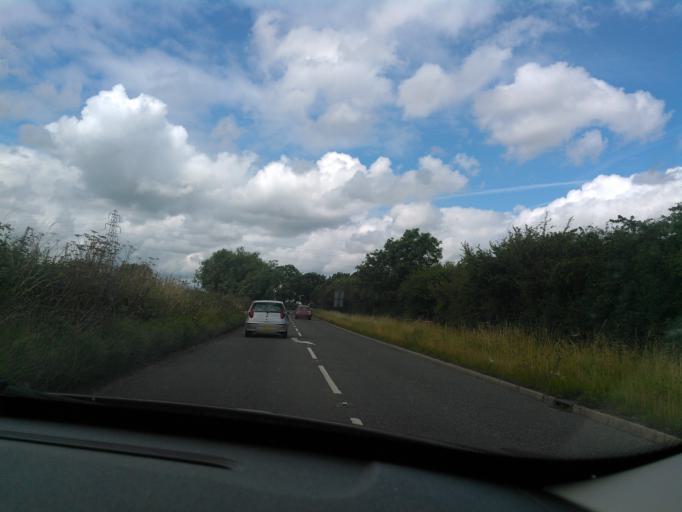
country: GB
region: England
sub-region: Derbyshire
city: Repton
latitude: 52.8580
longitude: -1.5649
